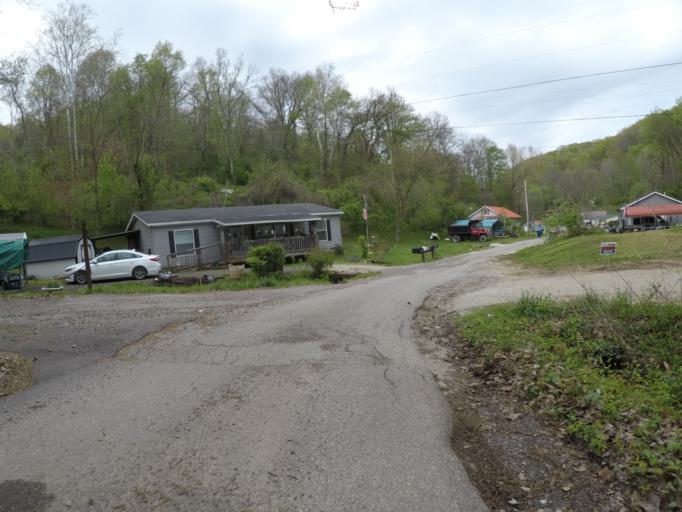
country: US
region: West Virginia
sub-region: Cabell County
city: Huntington
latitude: 38.3907
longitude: -82.4862
